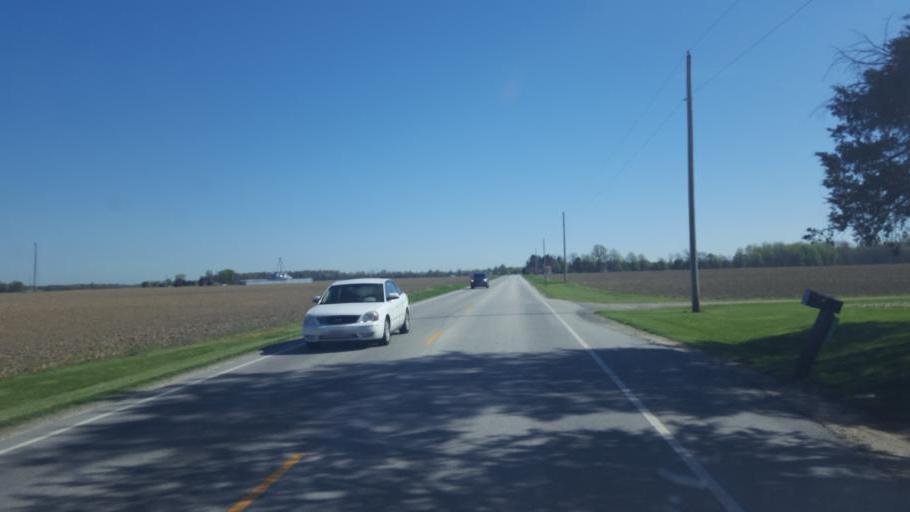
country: US
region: Ohio
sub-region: Wyandot County
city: Upper Sandusky
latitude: 40.9386
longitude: -83.1893
